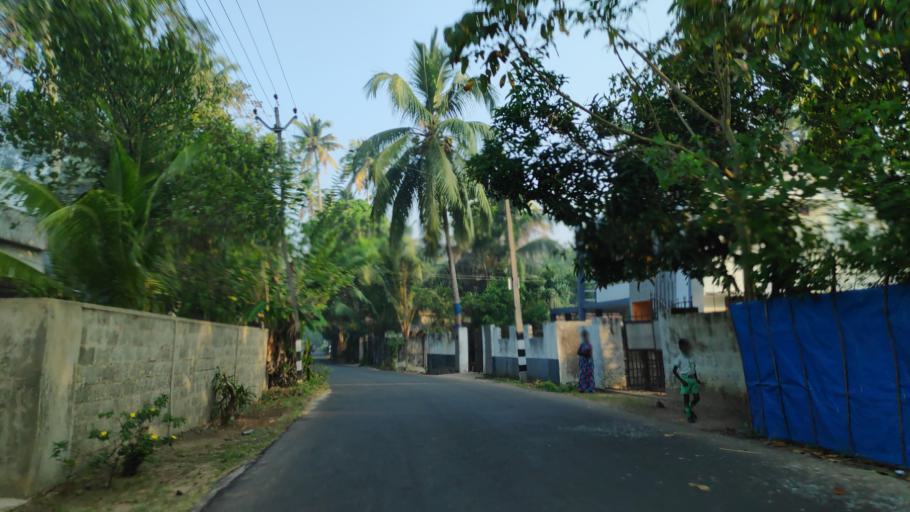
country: IN
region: Kerala
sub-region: Alappuzha
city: Vayalar
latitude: 9.6949
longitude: 76.2903
